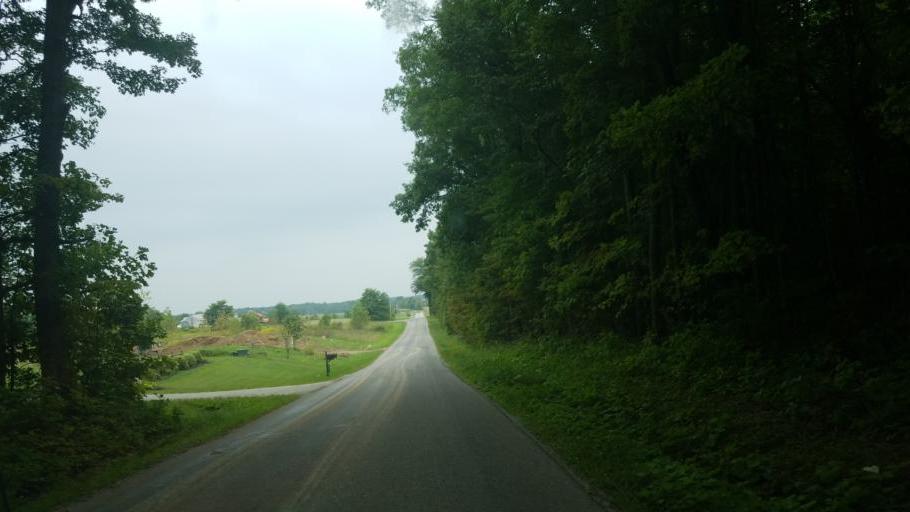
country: US
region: Ohio
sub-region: Medina County
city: Westfield Center
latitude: 40.9590
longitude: -81.9669
